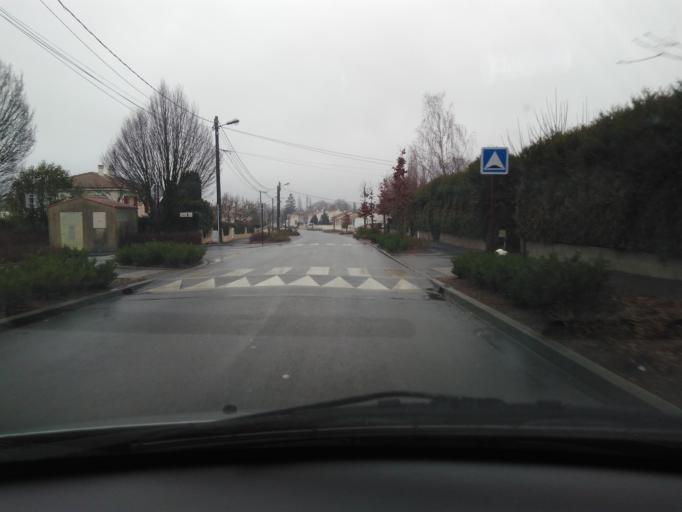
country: FR
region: Pays de la Loire
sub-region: Departement de la Vendee
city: La Ferriere
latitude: 46.7065
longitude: -1.3100
